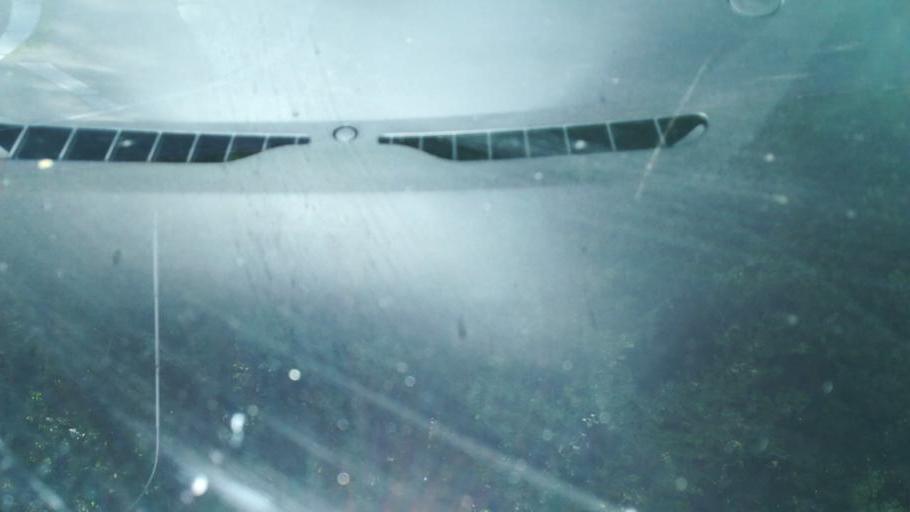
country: DE
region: Baden-Wuerttemberg
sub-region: Freiburg Region
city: Singen
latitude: 47.7694
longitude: 8.8464
